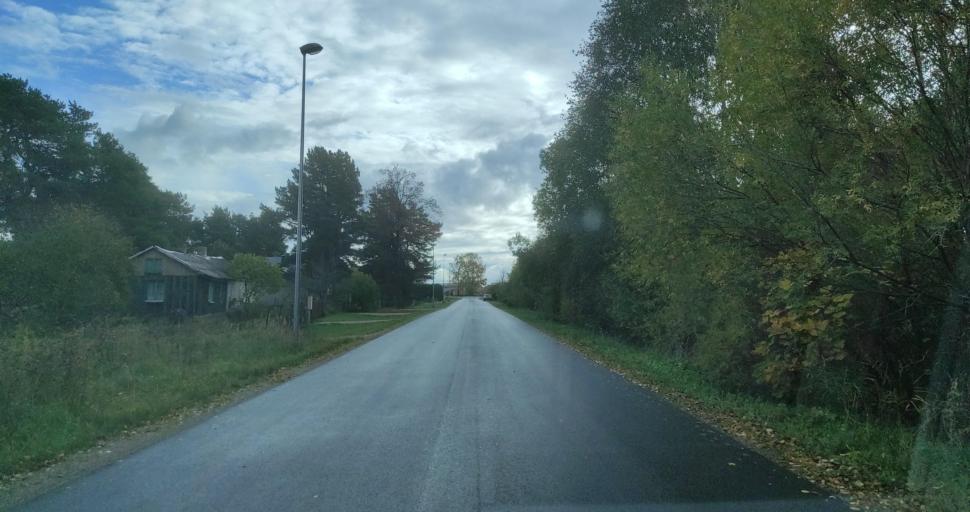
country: LV
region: Skrunda
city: Skrunda
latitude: 56.6833
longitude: 22.0120
